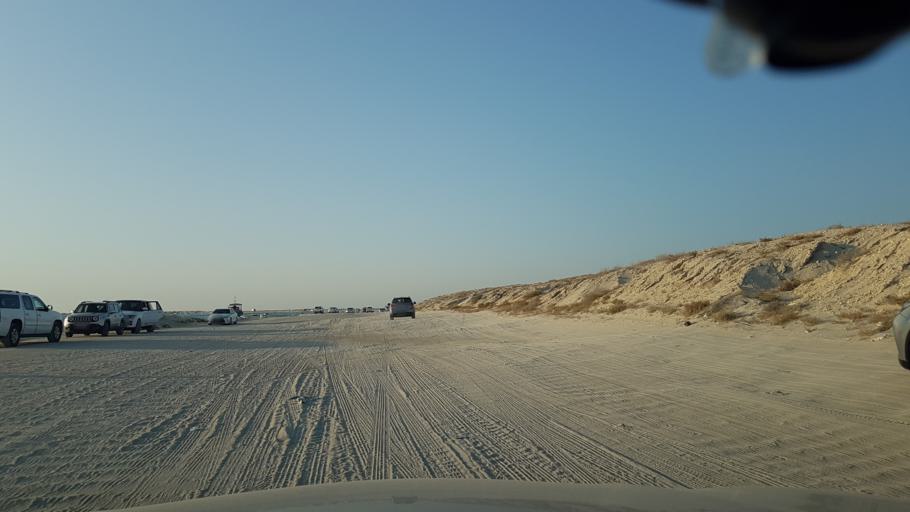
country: BH
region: Manama
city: Jidd Hafs
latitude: 26.2462
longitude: 50.5027
